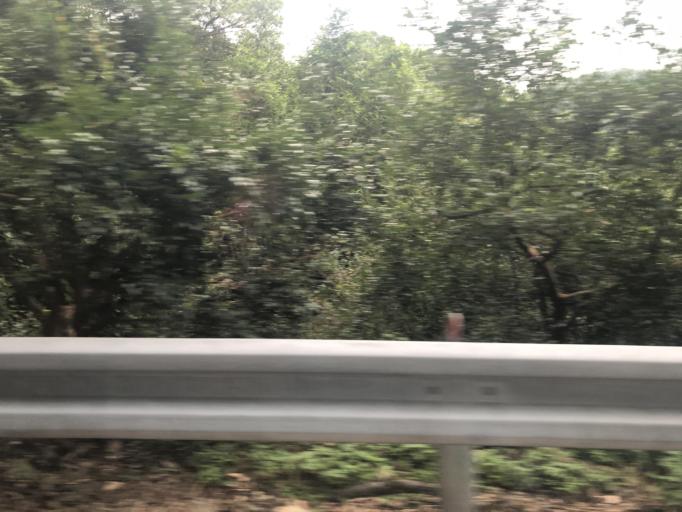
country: TW
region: Taiwan
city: Daxi
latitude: 24.8823
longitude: 121.4186
